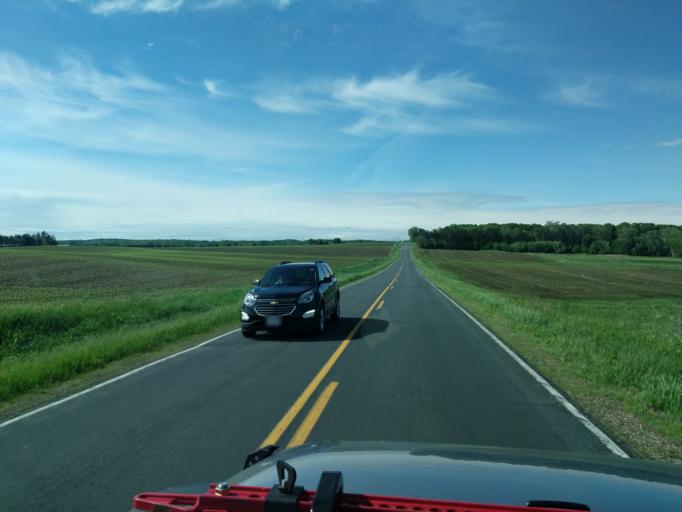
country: US
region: Wisconsin
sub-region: Saint Croix County
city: Hammond
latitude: 44.8742
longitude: -92.4969
